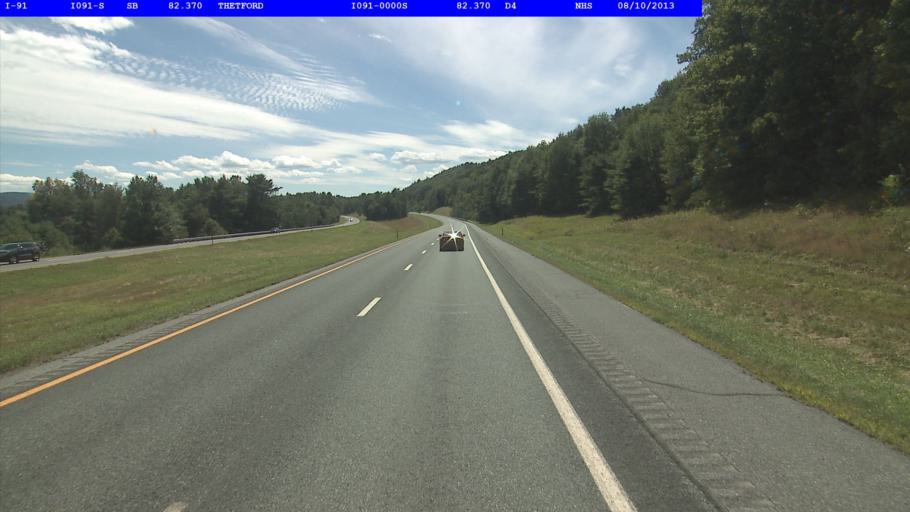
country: US
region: New Hampshire
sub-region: Grafton County
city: Lyme
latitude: 43.7877
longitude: -72.2159
